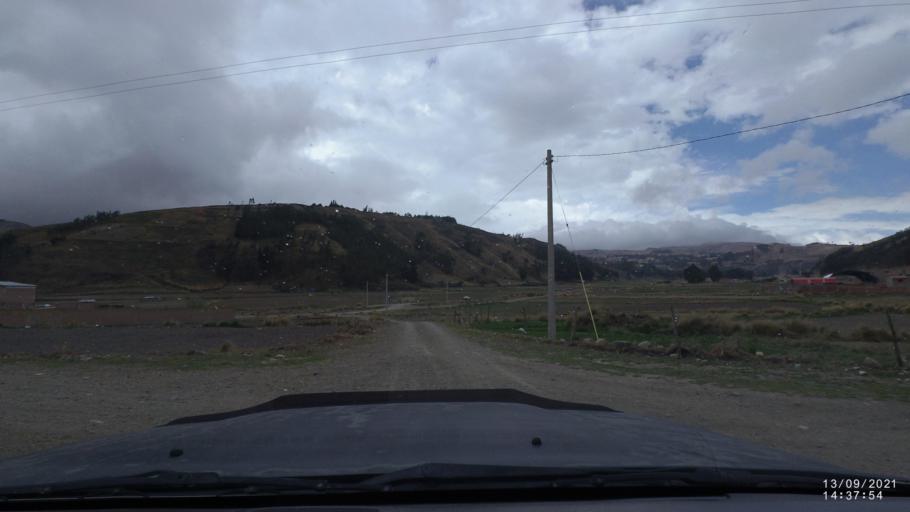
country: BO
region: Cochabamba
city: Colomi
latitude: -17.3710
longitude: -65.8337
